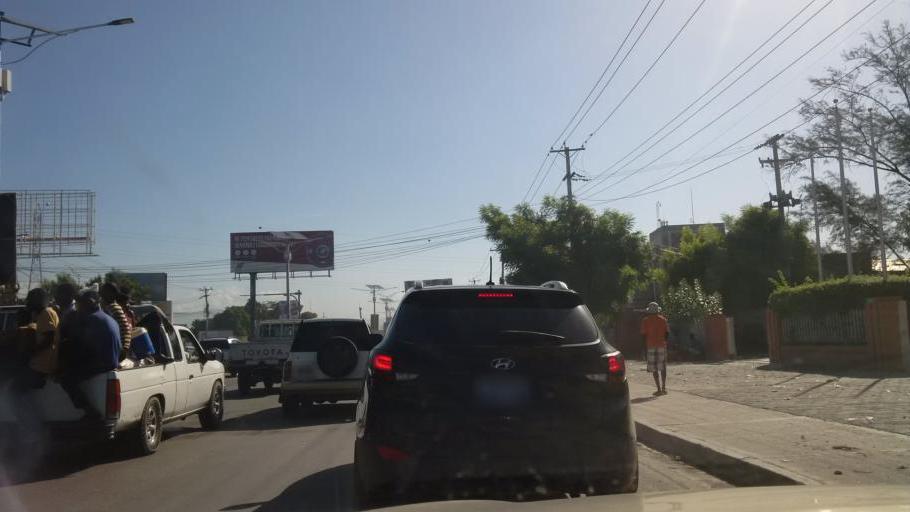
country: HT
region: Ouest
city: Delmas 73
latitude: 18.5650
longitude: -72.3139
